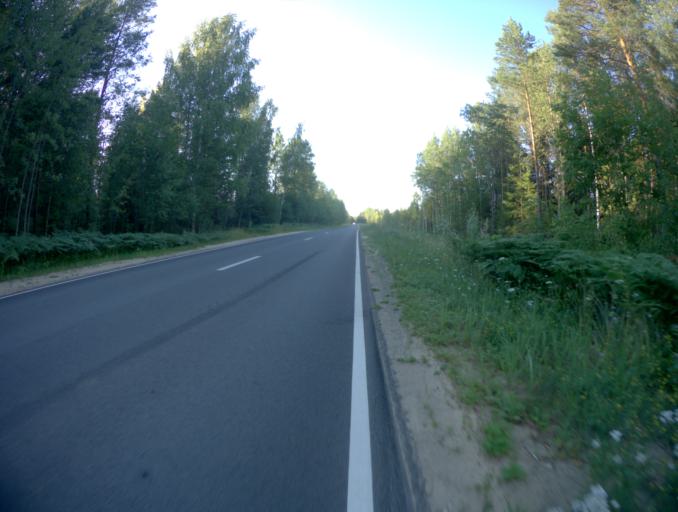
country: RU
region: Vladimir
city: Galitsy
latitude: 56.1231
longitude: 42.8731
